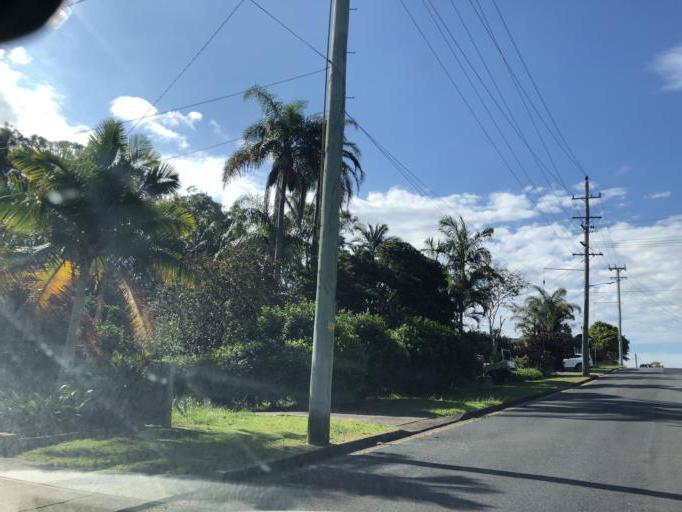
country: AU
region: New South Wales
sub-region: Coffs Harbour
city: Moonee Beach
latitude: -30.2348
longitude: 153.1489
